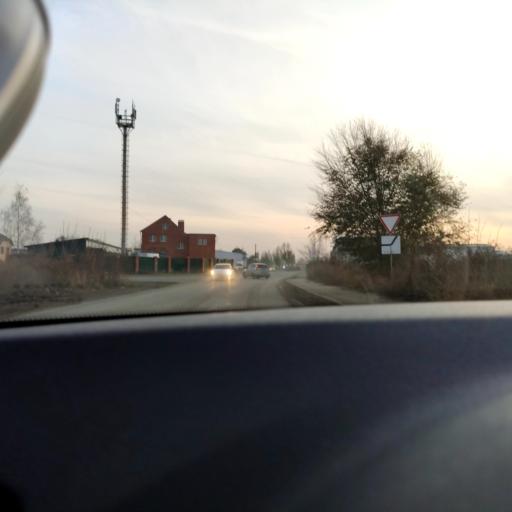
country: RU
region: Samara
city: Petra-Dubrava
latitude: 53.2555
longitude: 50.3118
